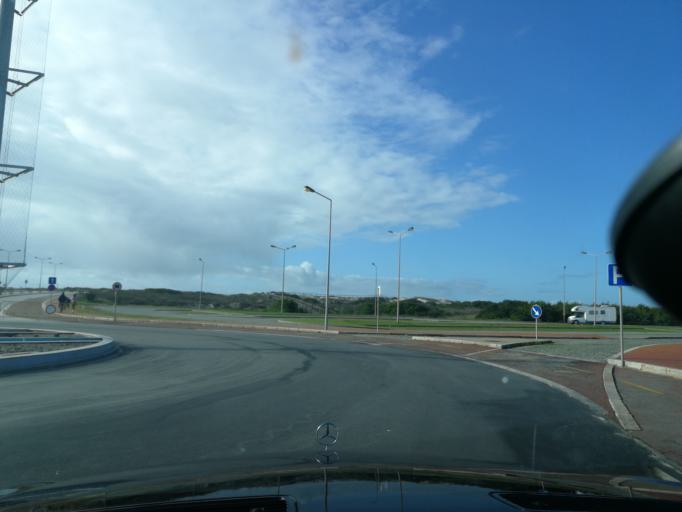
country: PT
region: Aveiro
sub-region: Murtosa
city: Murtosa
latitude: 40.7646
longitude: -8.7083
